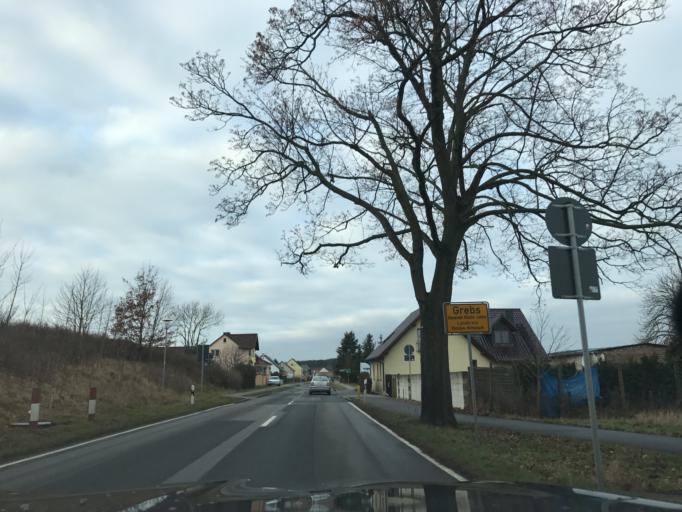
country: DE
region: Brandenburg
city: Golzow
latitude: 52.3395
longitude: 12.6681
